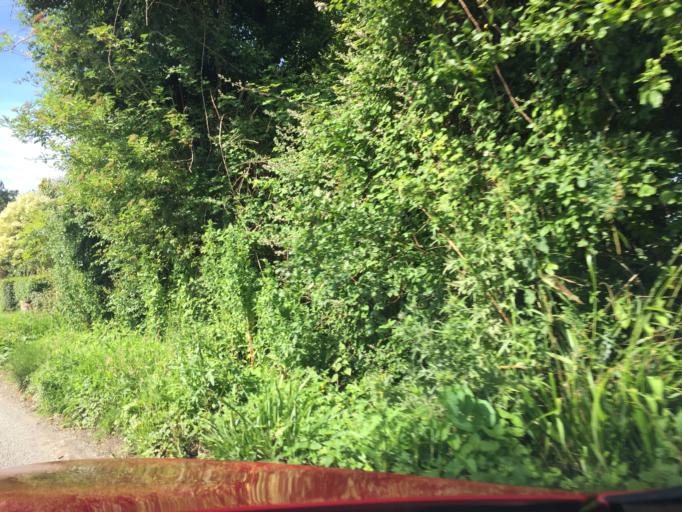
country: GB
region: England
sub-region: Gloucestershire
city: Stonehouse
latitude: 51.7980
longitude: -2.3442
